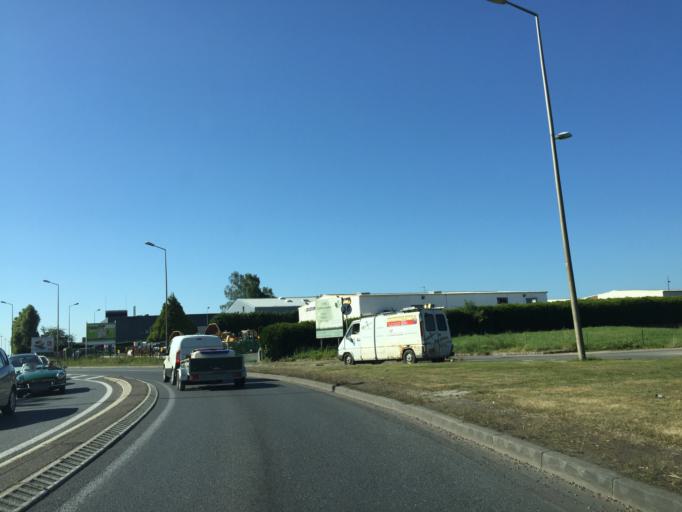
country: FR
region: Lower Normandy
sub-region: Departement du Calvados
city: Beuvillers
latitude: 49.1452
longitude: 0.2629
